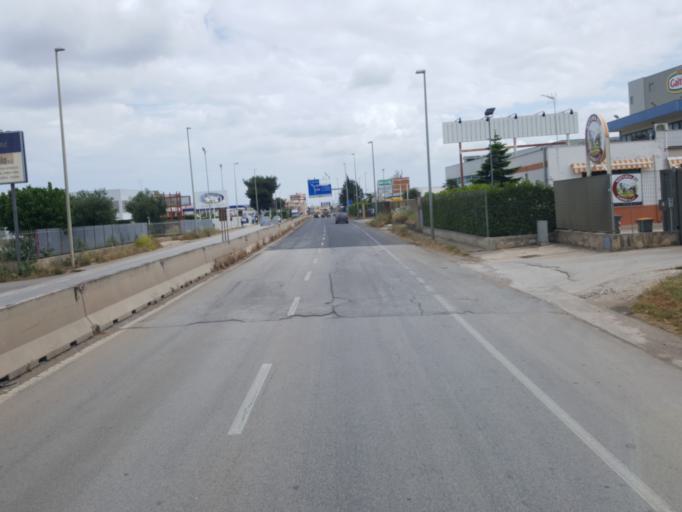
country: IT
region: Apulia
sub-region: Provincia di Bari
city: Modugno
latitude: 41.0893
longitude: 16.7654
